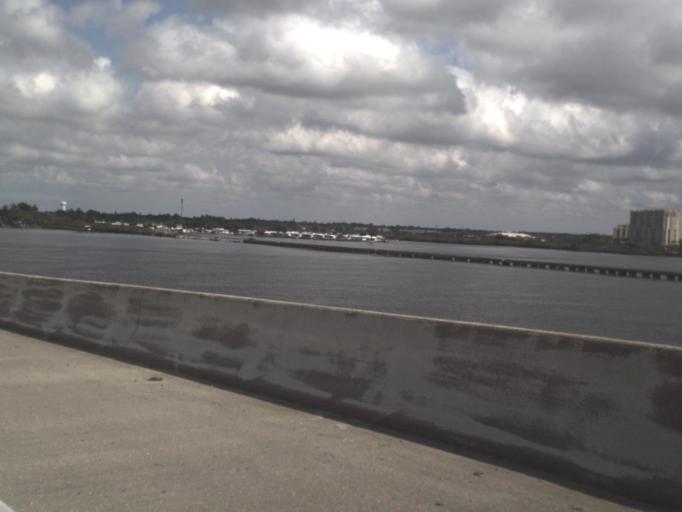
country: US
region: Florida
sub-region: Manatee County
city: Bradenton
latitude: 27.5031
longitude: -82.5712
